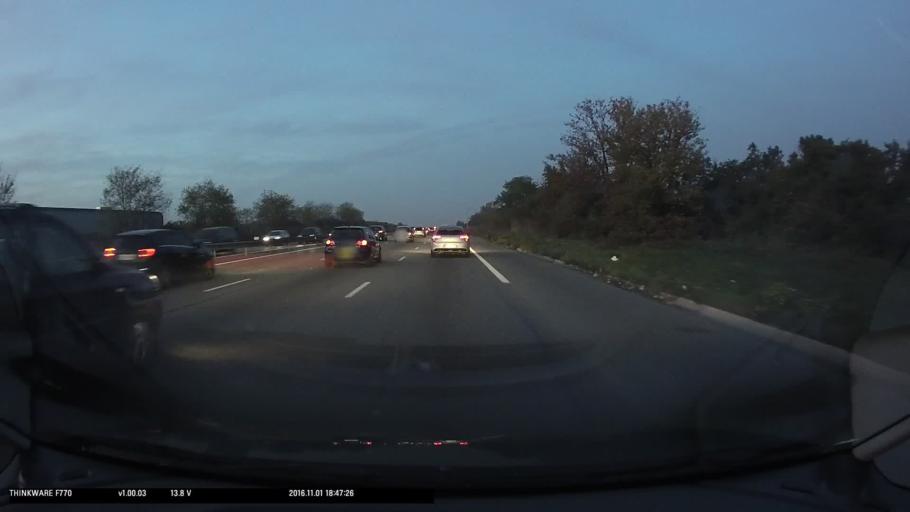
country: FR
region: Ile-de-France
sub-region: Departement de l'Essonne
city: Chilly-Mazarin
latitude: 48.7201
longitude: 2.3111
